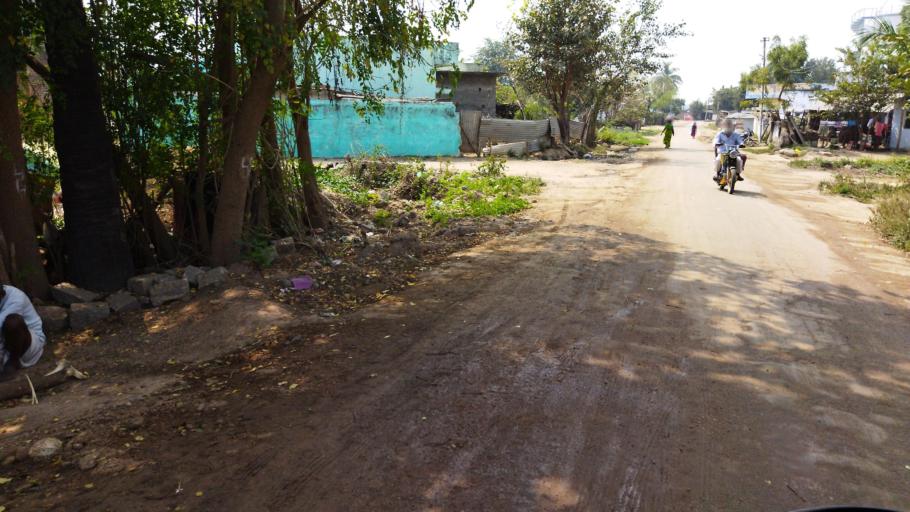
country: IN
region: Telangana
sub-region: Nalgonda
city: Nalgonda
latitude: 17.1420
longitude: 79.3905
